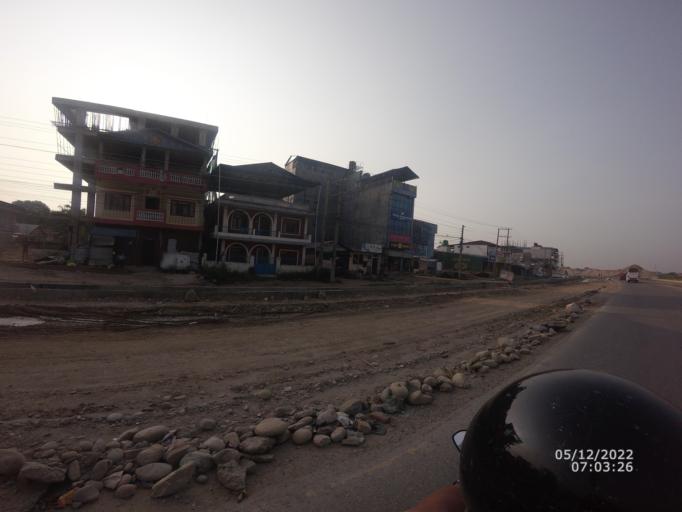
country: NP
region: Central Region
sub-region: Narayani Zone
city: Bharatpur
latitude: 27.6767
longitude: 84.4308
